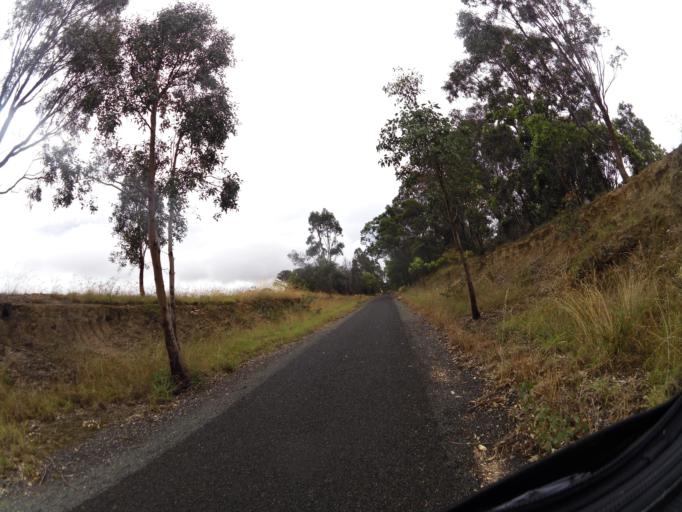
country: AU
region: Victoria
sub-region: East Gippsland
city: Bairnsdale
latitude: -37.8196
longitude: 147.7210
